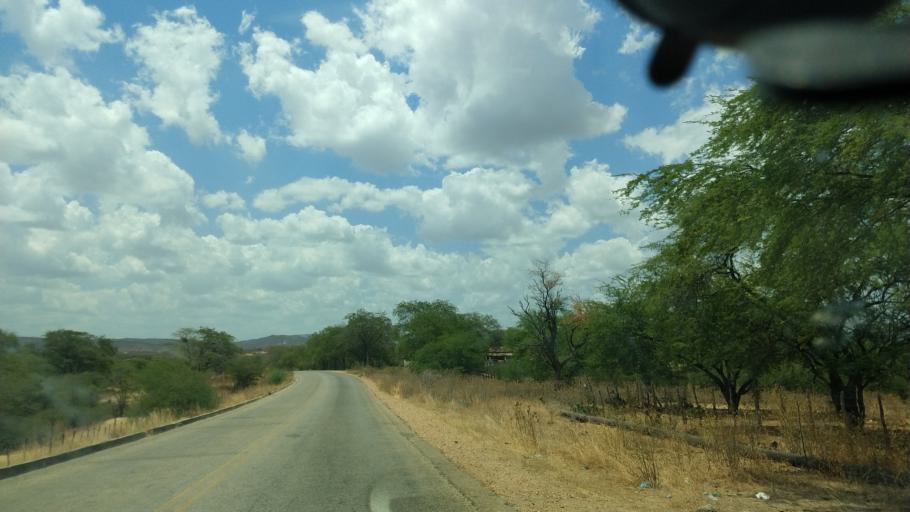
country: BR
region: Rio Grande do Norte
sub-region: Currais Novos
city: Currais Novos
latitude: -6.2765
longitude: -36.5394
